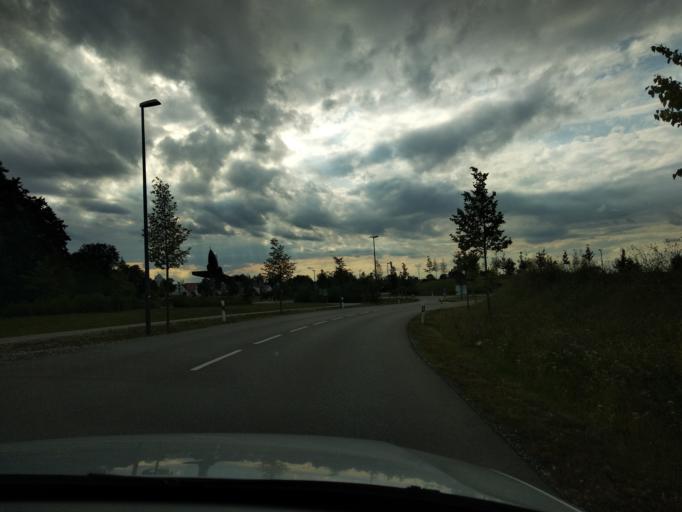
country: DE
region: Bavaria
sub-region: Swabia
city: Memmingerberg
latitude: 47.9907
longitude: 10.2191
